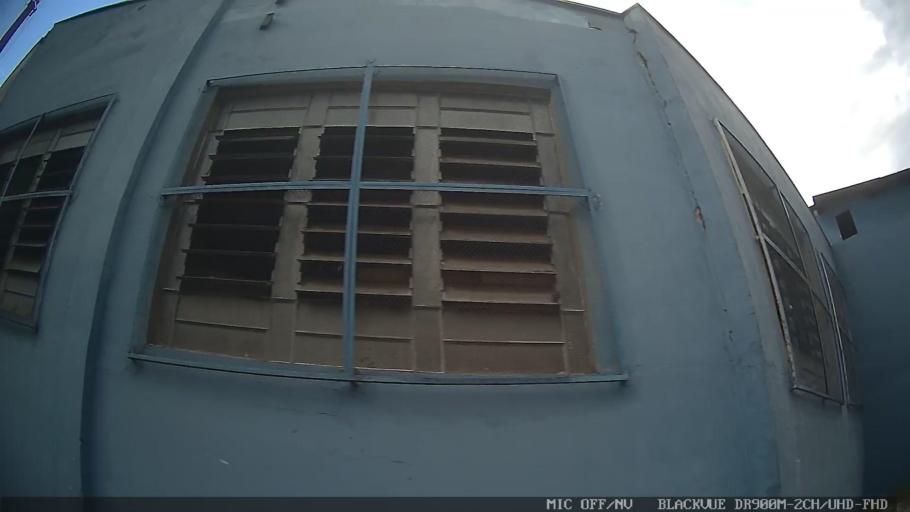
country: BR
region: Sao Paulo
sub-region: Pedreira
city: Pedreira
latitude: -22.7277
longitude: -46.8949
